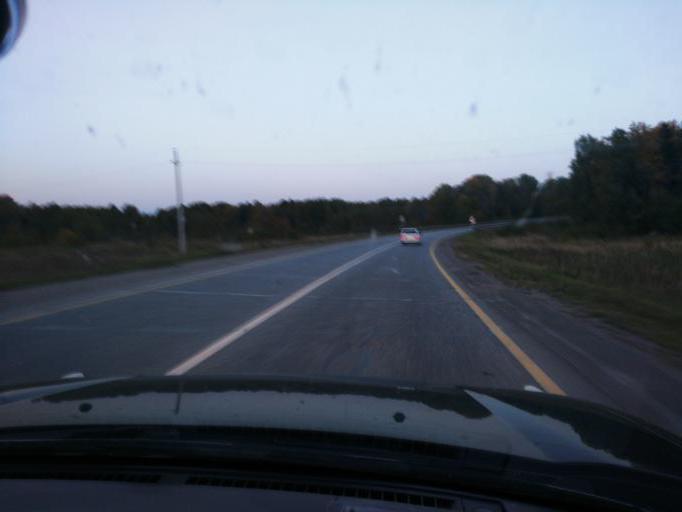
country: RU
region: Perm
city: Verkhnechusovskiye Gorodki
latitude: 58.2935
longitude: 56.8902
